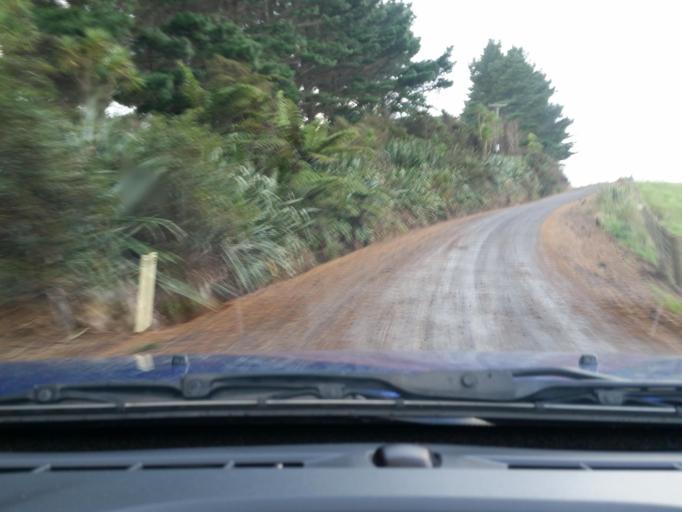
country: NZ
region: Northland
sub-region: Kaipara District
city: Dargaville
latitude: -35.7575
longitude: 173.6122
